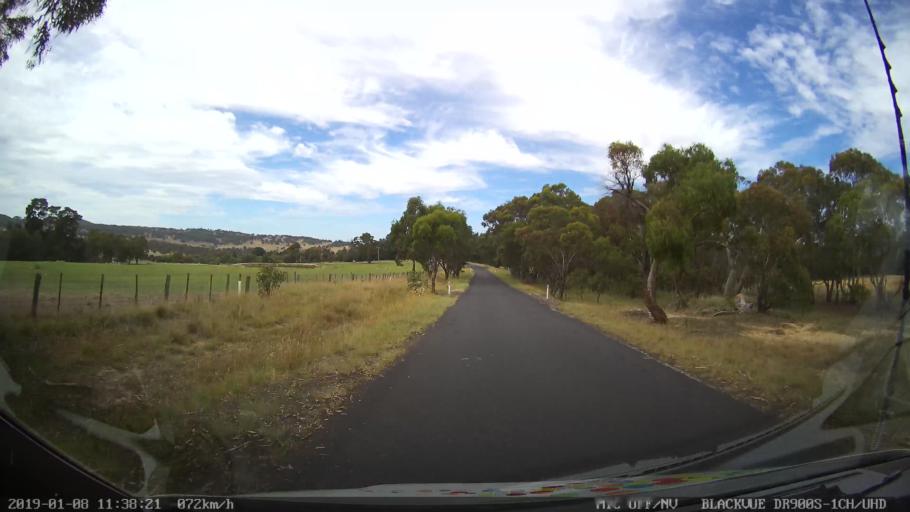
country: AU
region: New South Wales
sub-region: Guyra
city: Guyra
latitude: -30.3598
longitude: 151.5552
